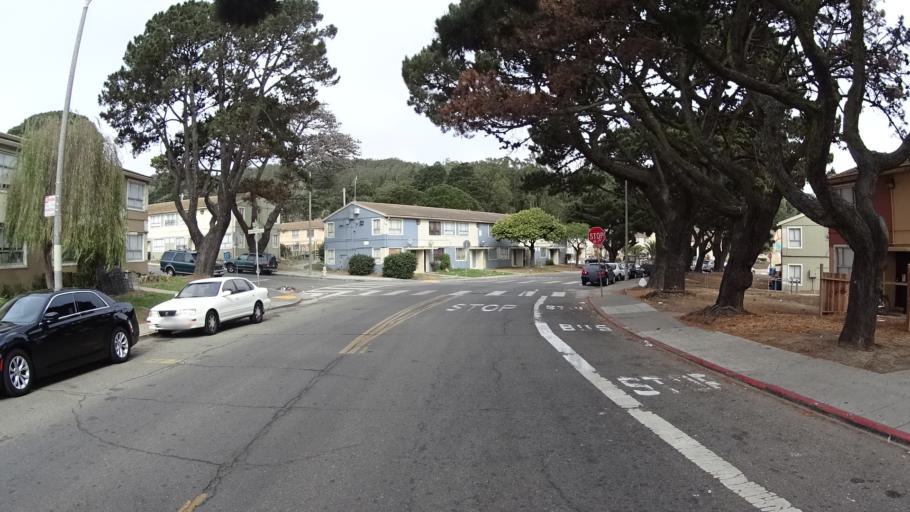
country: US
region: California
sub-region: San Mateo County
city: Brisbane
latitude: 37.7117
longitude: -122.4188
